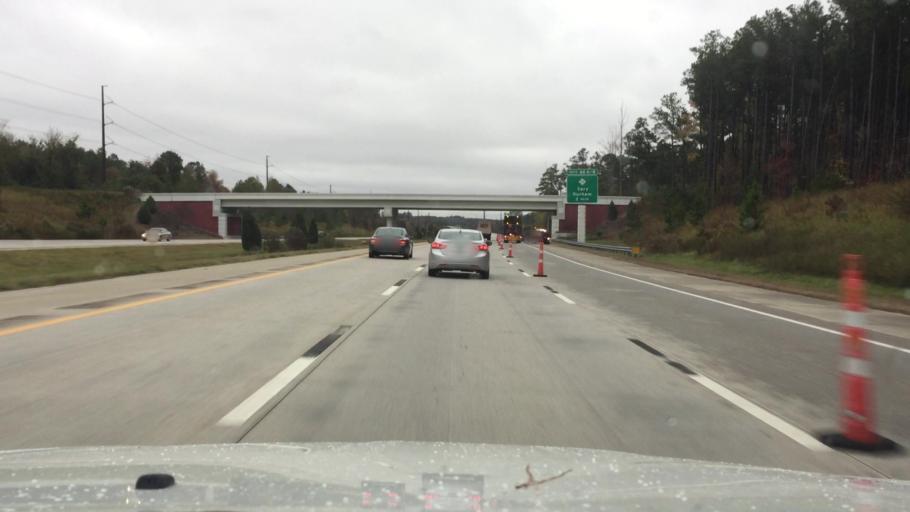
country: US
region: North Carolina
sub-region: Wake County
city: Green Level
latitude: 35.8077
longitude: -78.8921
